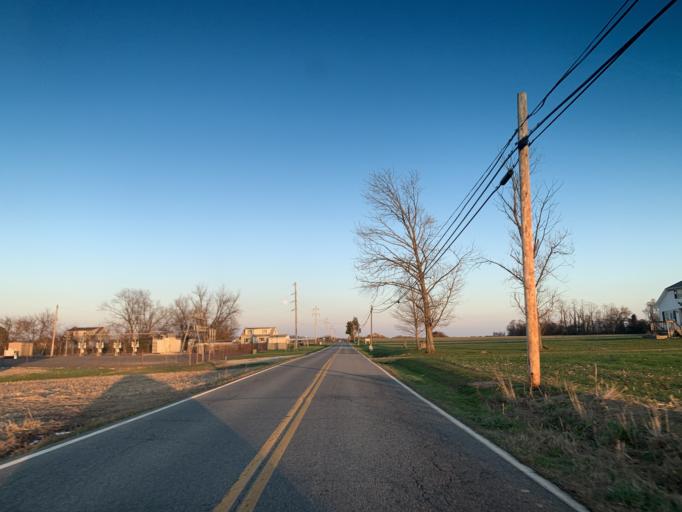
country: US
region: Maryland
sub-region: Cecil County
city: Charlestown
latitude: 39.4101
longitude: -75.9192
